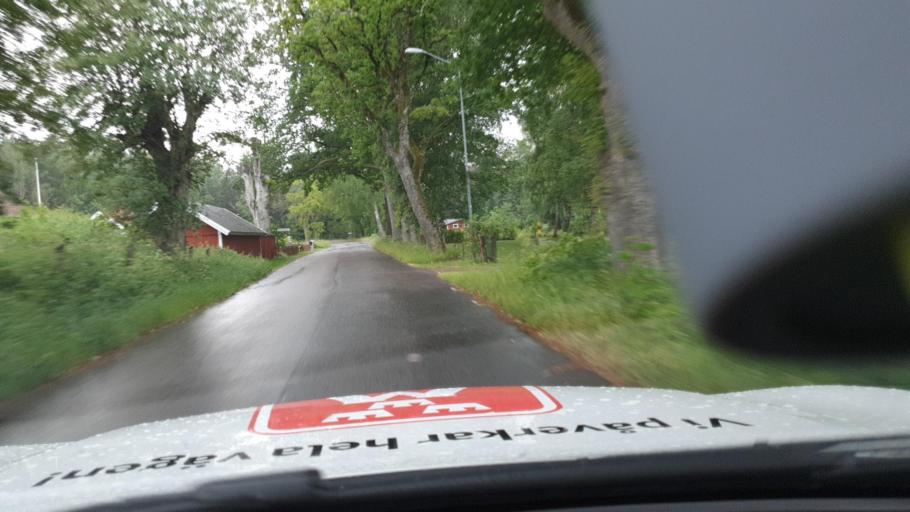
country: SE
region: Vaestra Goetaland
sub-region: Skovde Kommun
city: Stopen
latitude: 58.4251
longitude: 13.9147
